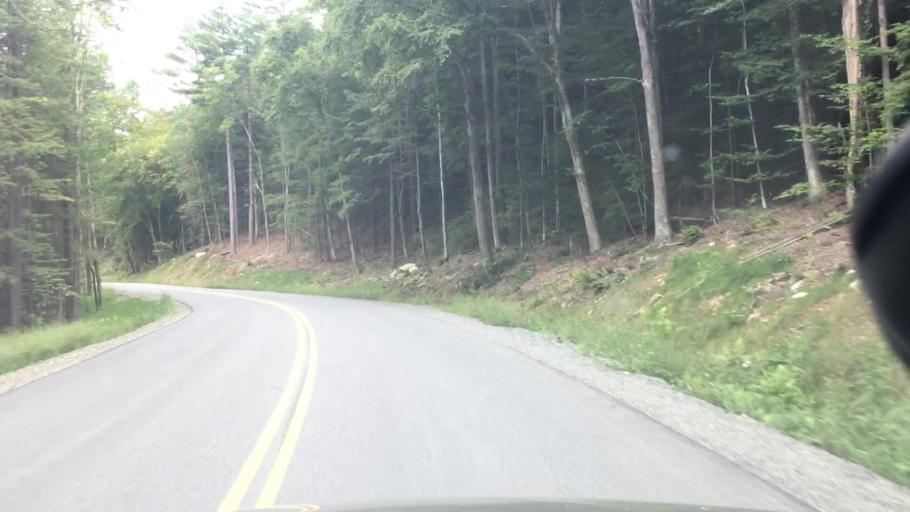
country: US
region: Massachusetts
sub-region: Franklin County
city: Colrain
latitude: 42.7763
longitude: -72.7673
